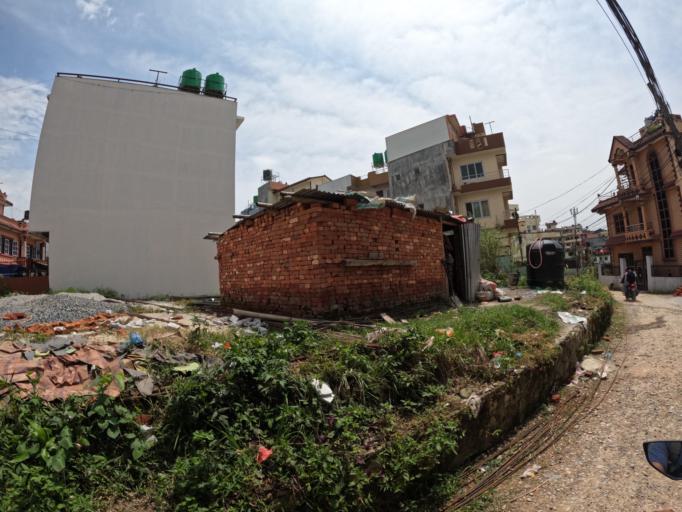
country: NP
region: Central Region
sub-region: Bagmati Zone
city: Kathmandu
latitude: 27.6799
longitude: 85.3691
